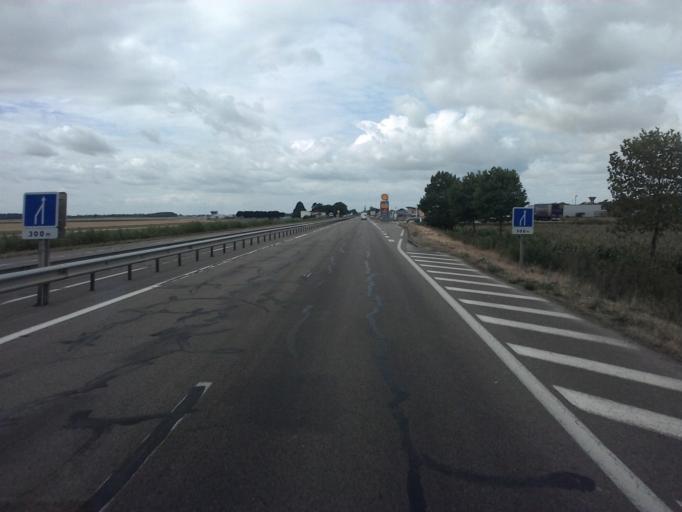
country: FR
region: Franche-Comte
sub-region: Departement du Jura
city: Tavaux
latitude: 47.0495
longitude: 5.4308
